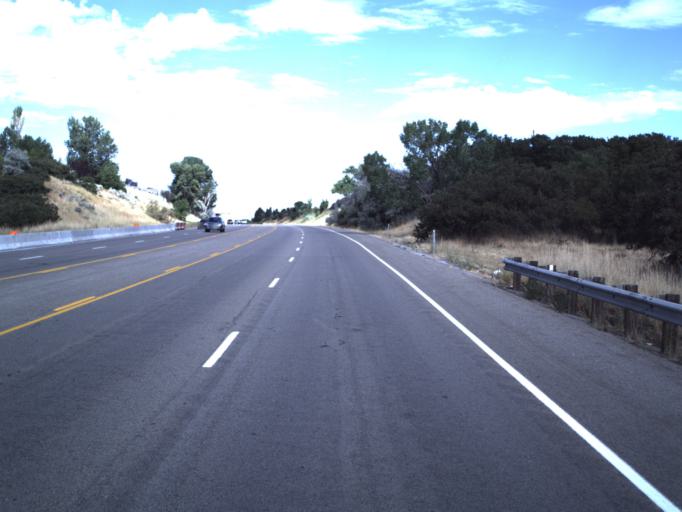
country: US
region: Utah
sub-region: Weber County
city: Uintah
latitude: 41.1606
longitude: -111.9468
